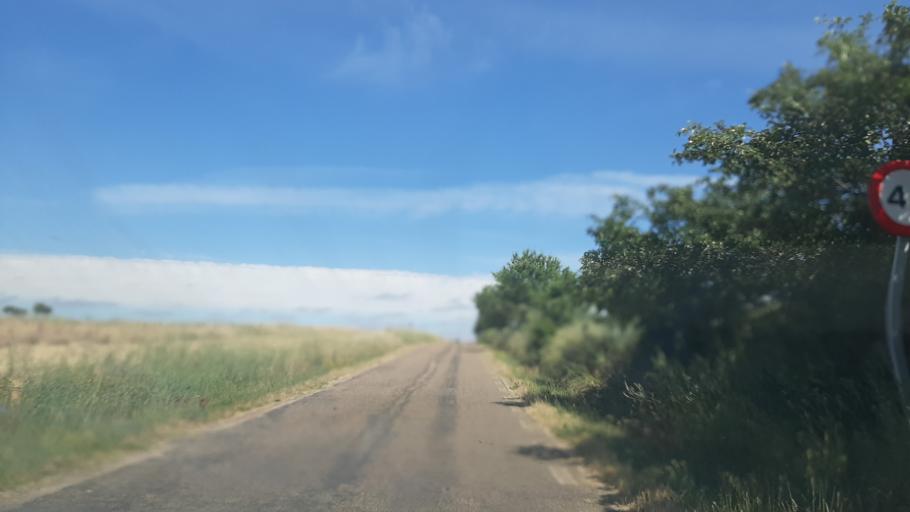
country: ES
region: Castille and Leon
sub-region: Provincia de Salamanca
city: Zamarra
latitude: 40.5217
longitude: -6.4546
